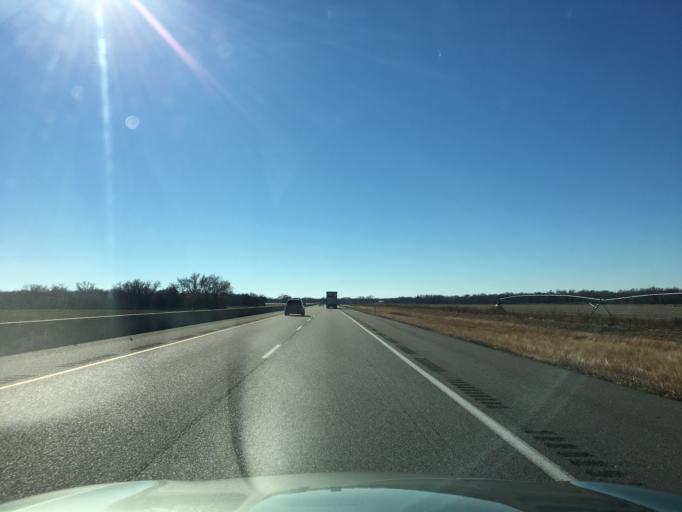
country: US
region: Kansas
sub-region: Sumner County
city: Belle Plaine
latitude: 37.4044
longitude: -97.3245
